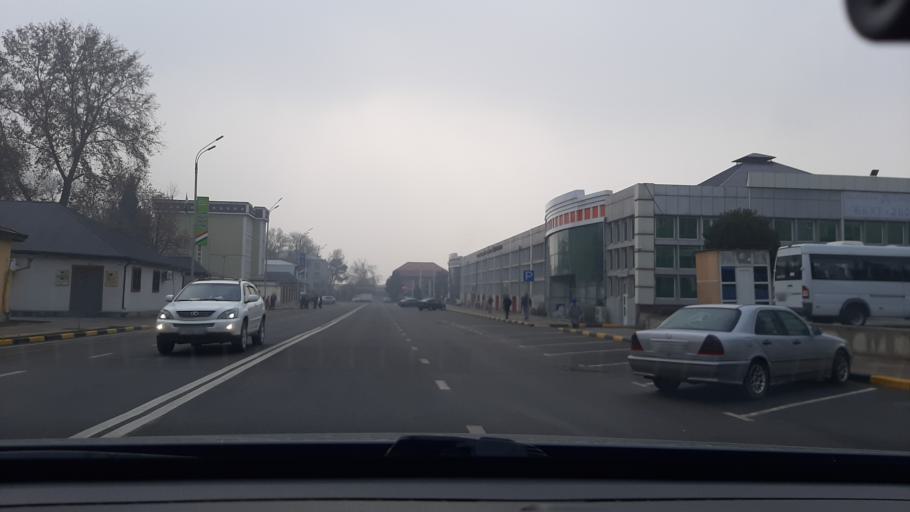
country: TJ
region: Dushanbe
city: Dushanbe
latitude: 38.5592
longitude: 68.7956
